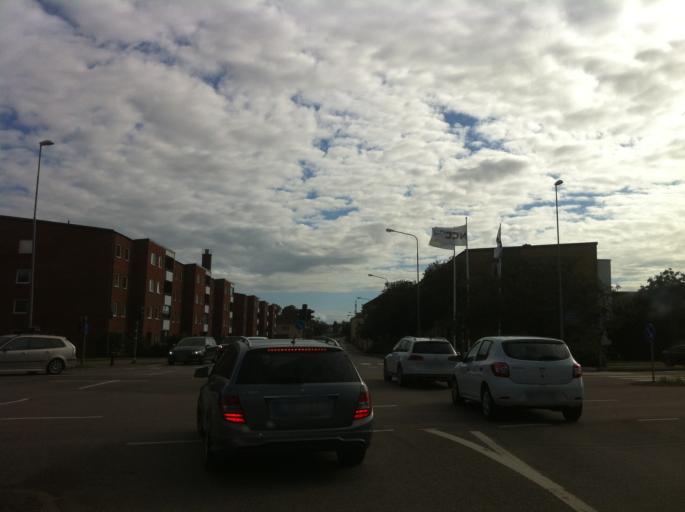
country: SE
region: Skane
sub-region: Bastads Kommun
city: Bastad
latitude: 56.3845
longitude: 12.9162
